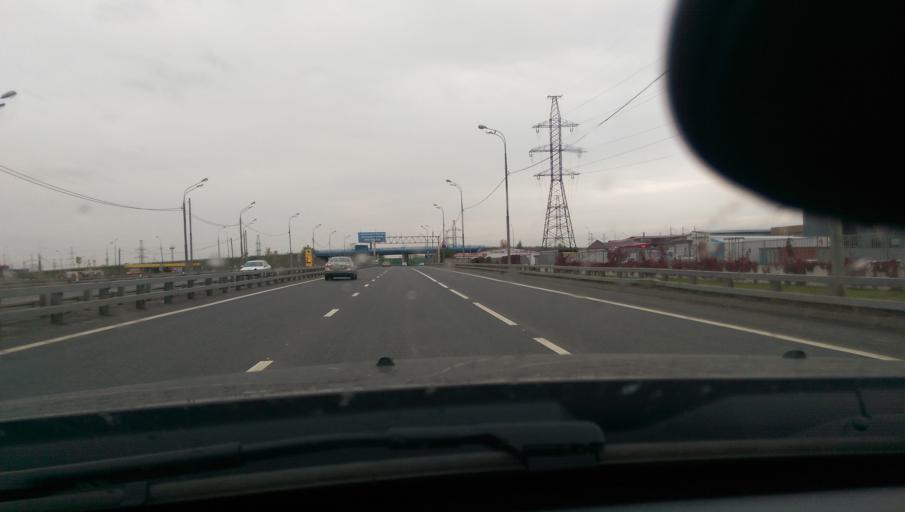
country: RU
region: Moscow
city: Vatutino
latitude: 55.9146
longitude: 37.6687
